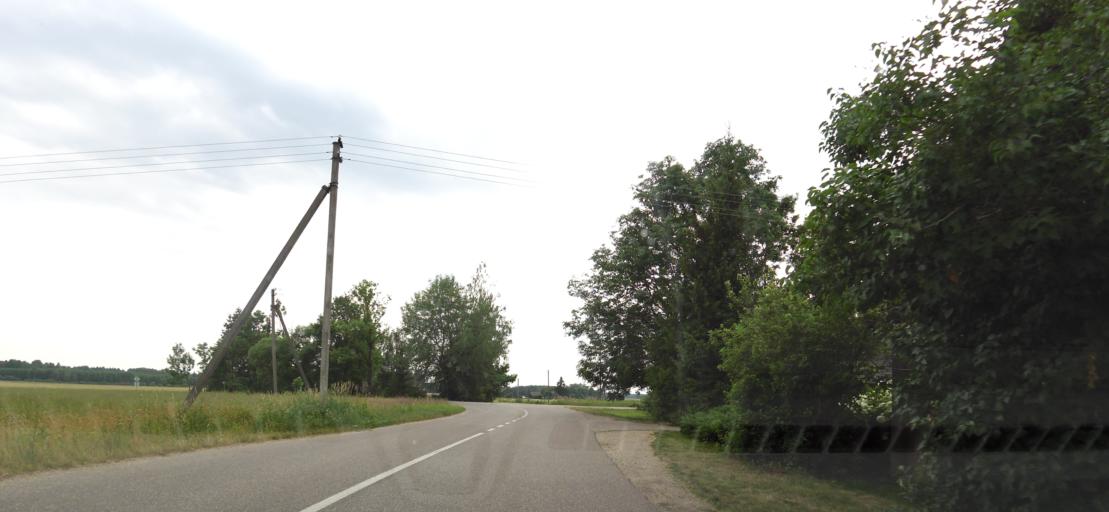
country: LT
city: Obeliai
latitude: 56.1368
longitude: 25.1237
